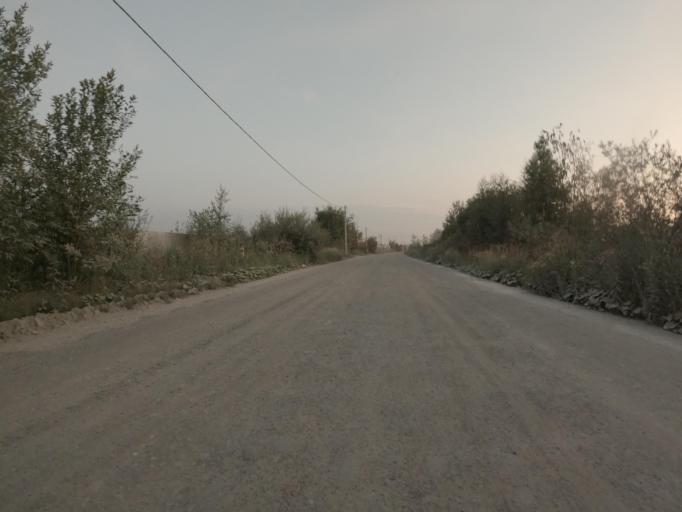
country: RU
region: Leningrad
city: Yanino Vtoroye
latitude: 59.9365
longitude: 30.5978
